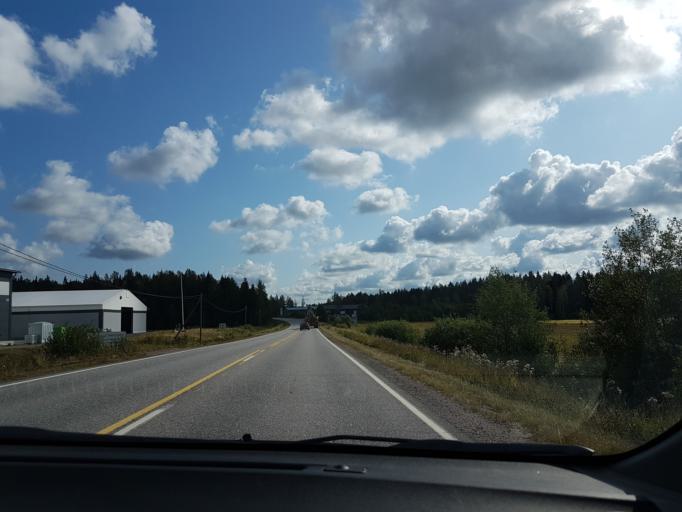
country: FI
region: Uusimaa
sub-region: Helsinki
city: Pornainen
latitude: 60.4735
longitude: 25.3082
